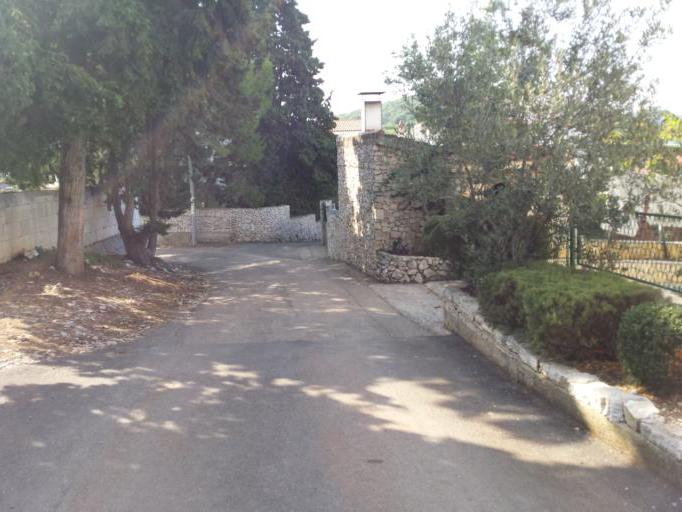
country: HR
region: Sibensko-Kniniska
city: Rogoznica
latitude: 43.5277
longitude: 15.9702
